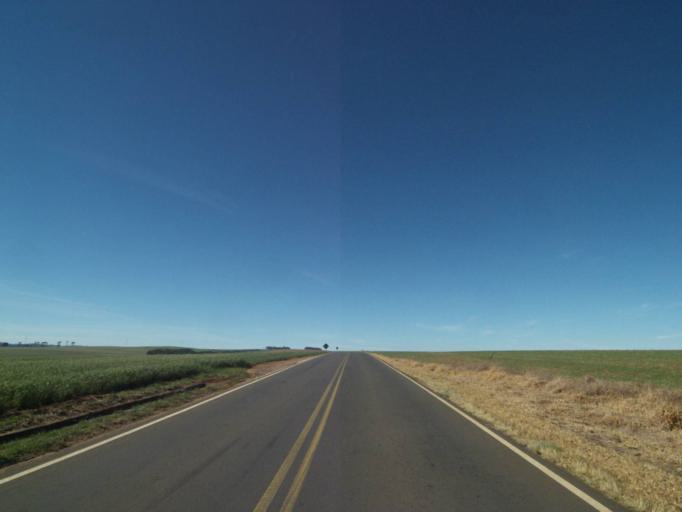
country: BR
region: Parana
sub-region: Tibagi
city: Tibagi
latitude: -24.5641
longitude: -50.2899
